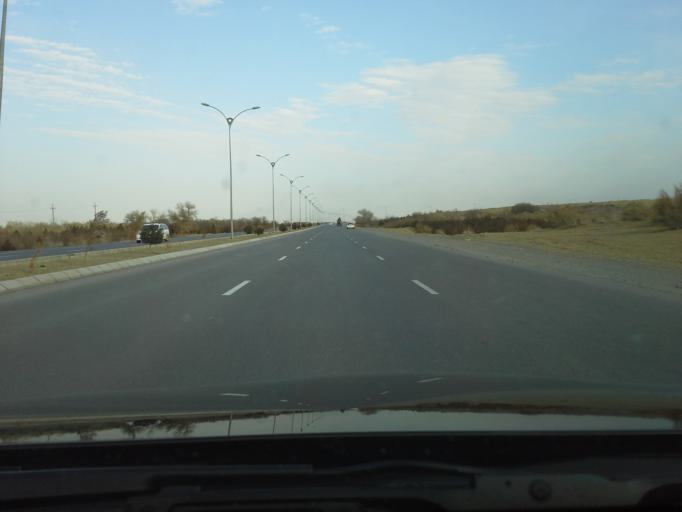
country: TM
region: Ahal
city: Abadan
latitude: 38.1039
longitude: 58.3248
